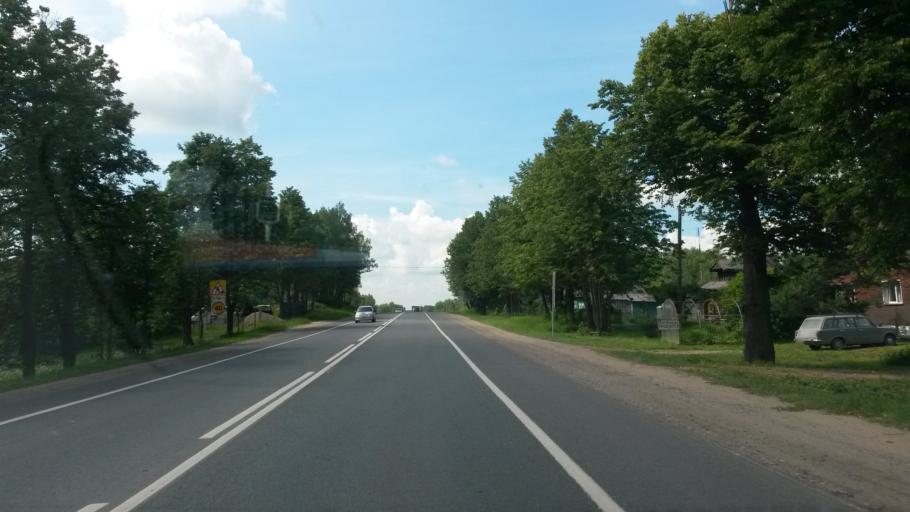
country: RU
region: Jaroslavl
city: Petrovsk
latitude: 56.8944
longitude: 39.1031
